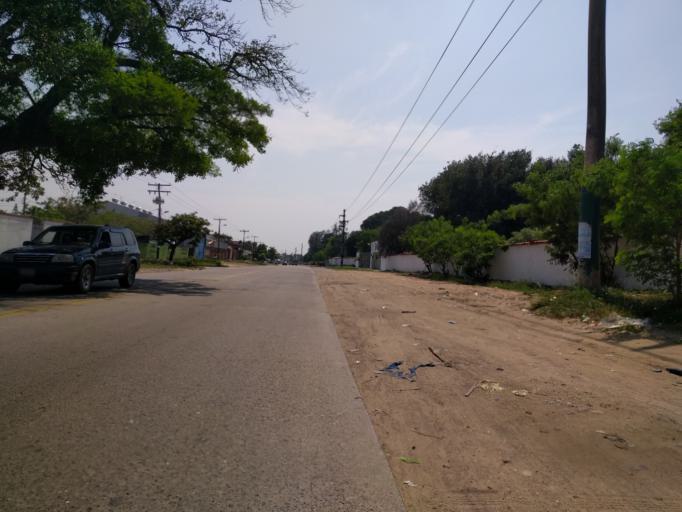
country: BO
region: Santa Cruz
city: Santa Cruz de la Sierra
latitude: -17.8029
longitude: -63.1632
